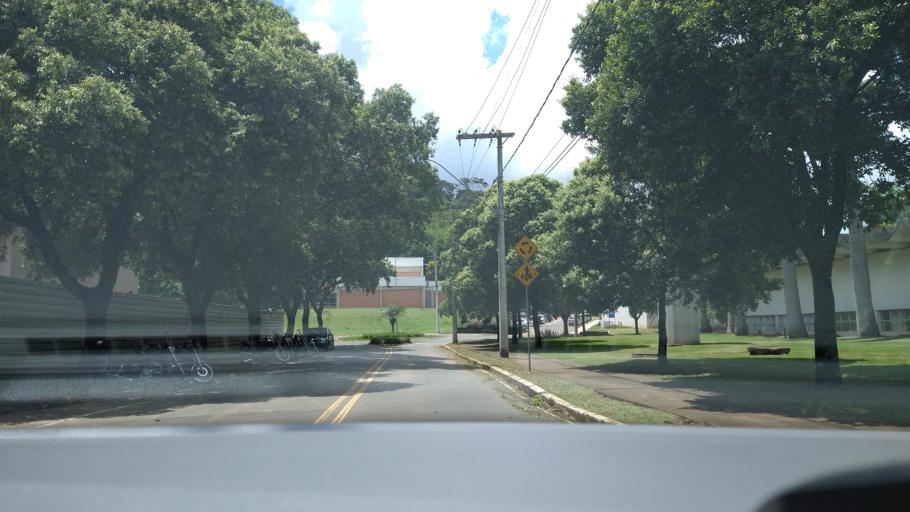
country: BR
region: Minas Gerais
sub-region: Vicosa
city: Vicosa
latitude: -20.7620
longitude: -42.8661
